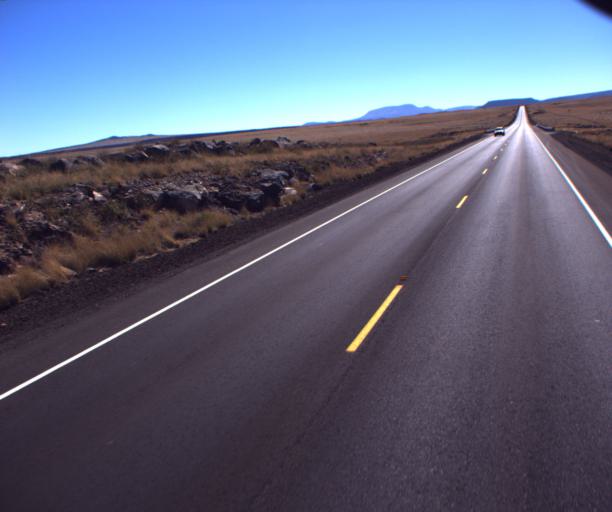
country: US
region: Arizona
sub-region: Apache County
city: Springerville
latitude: 34.2175
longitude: -109.3341
